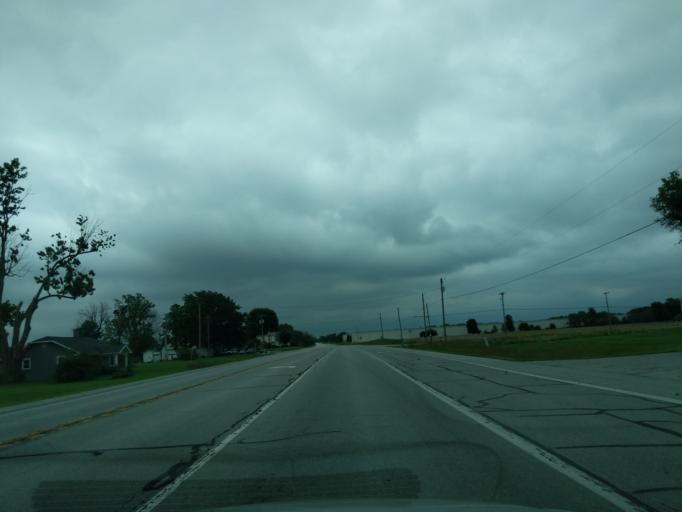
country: US
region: Indiana
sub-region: Madison County
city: Alexandria
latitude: 40.2774
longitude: -85.7297
